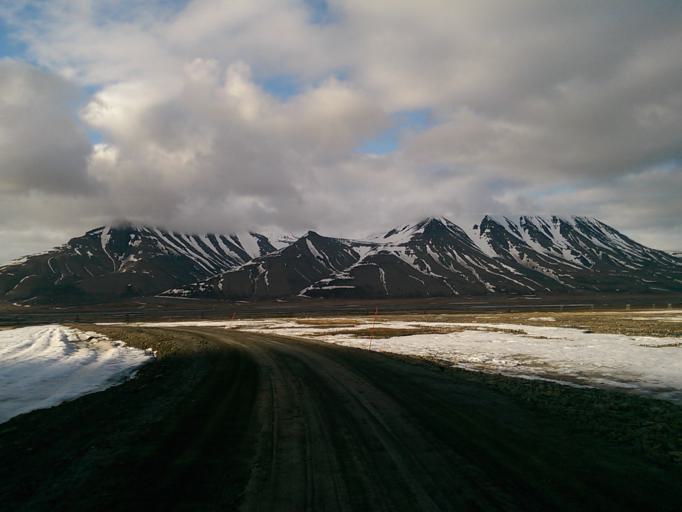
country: SJ
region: Svalbard
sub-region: Spitsbergen
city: Longyearbyen
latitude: 78.1885
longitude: 15.7835
